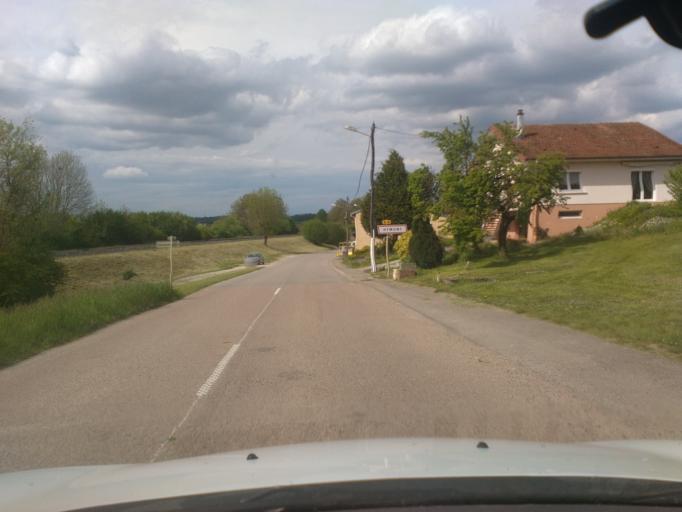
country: FR
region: Lorraine
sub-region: Departement des Vosges
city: Mirecourt
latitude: 48.2610
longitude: 6.1426
